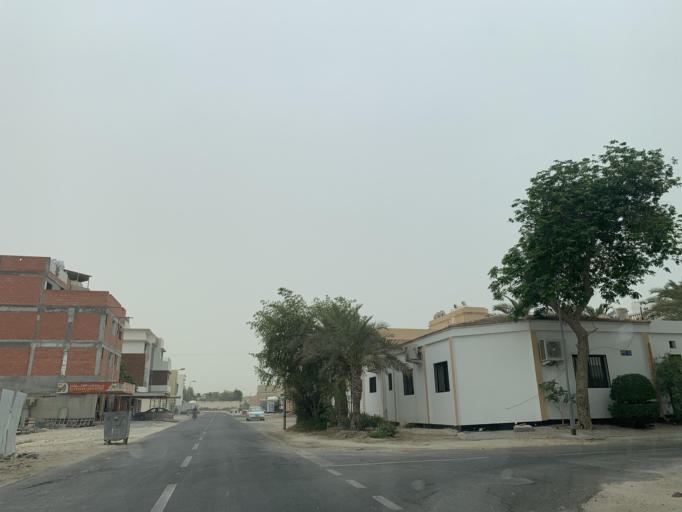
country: BH
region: Northern
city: Ar Rifa'
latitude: 26.1468
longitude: 50.5297
